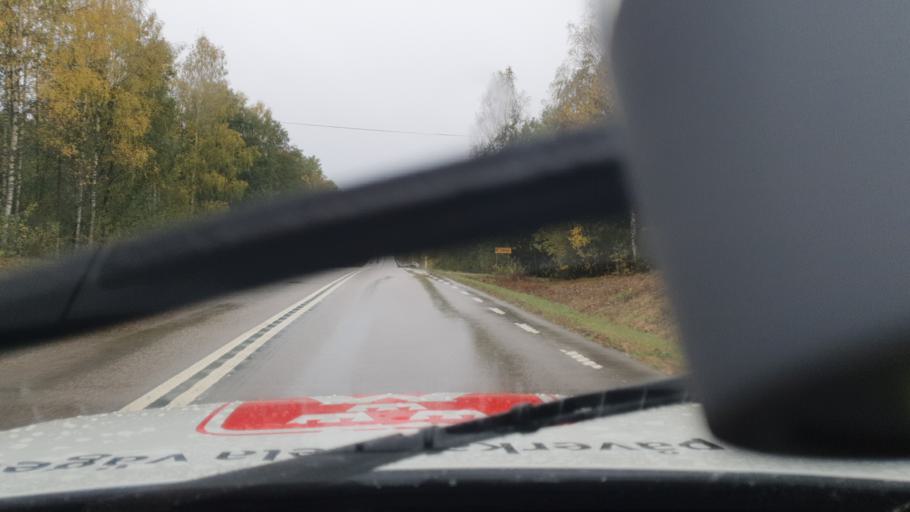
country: SE
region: Vaestra Goetaland
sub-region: Bengtsfors Kommun
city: Billingsfors
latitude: 58.9399
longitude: 12.1176
